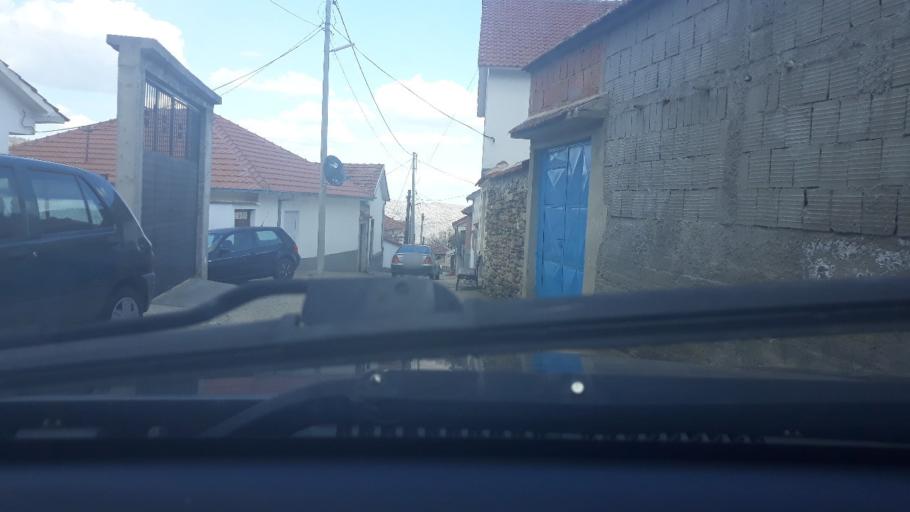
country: MK
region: Caska
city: Caska
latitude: 41.6411
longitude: 21.5872
